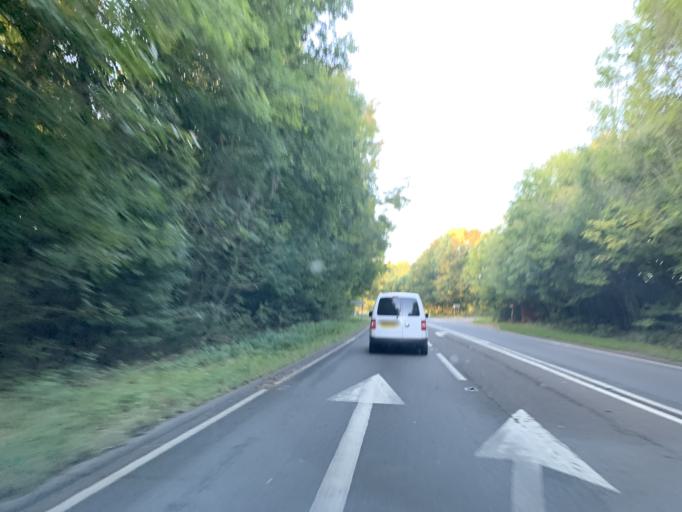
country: GB
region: England
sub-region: Wiltshire
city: Whiteparish
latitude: 50.9877
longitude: -1.6413
